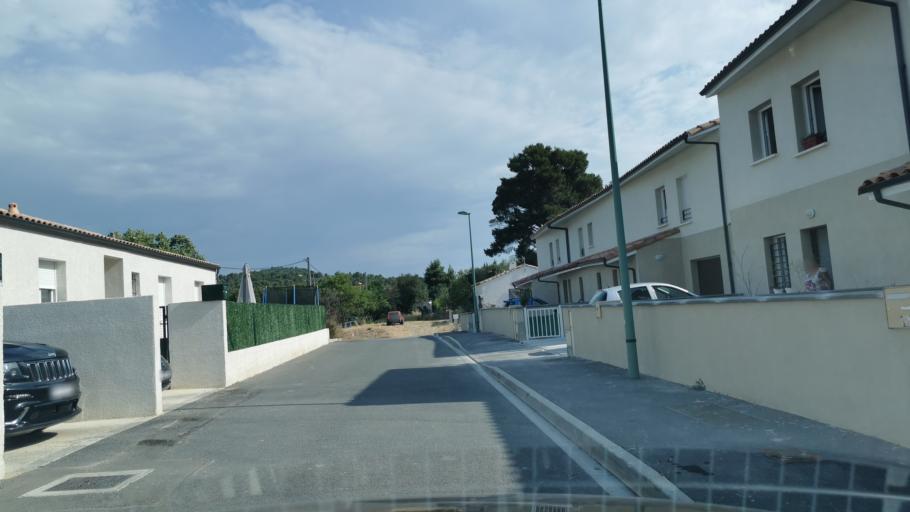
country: FR
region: Languedoc-Roussillon
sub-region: Departement de l'Aude
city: Bize-Minervois
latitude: 43.3139
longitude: 2.8724
